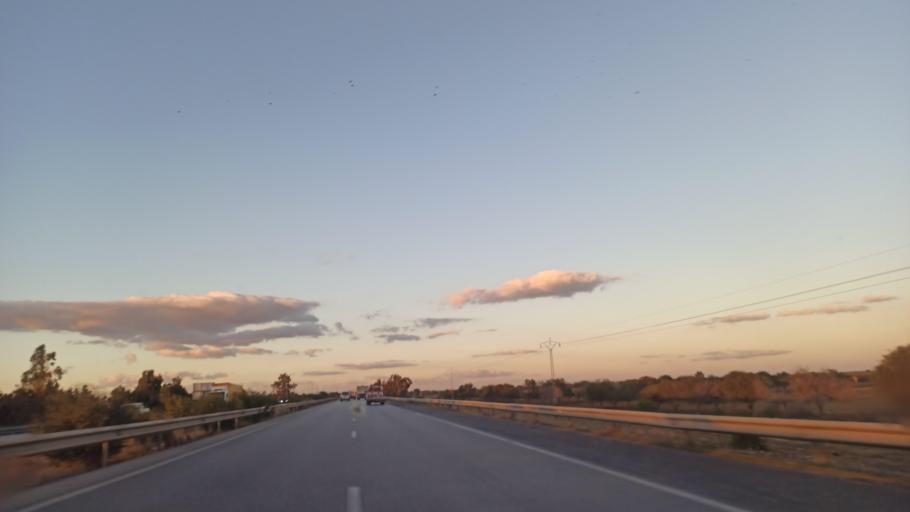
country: TN
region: Susah
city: Harqalah
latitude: 36.1265
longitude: 10.4063
